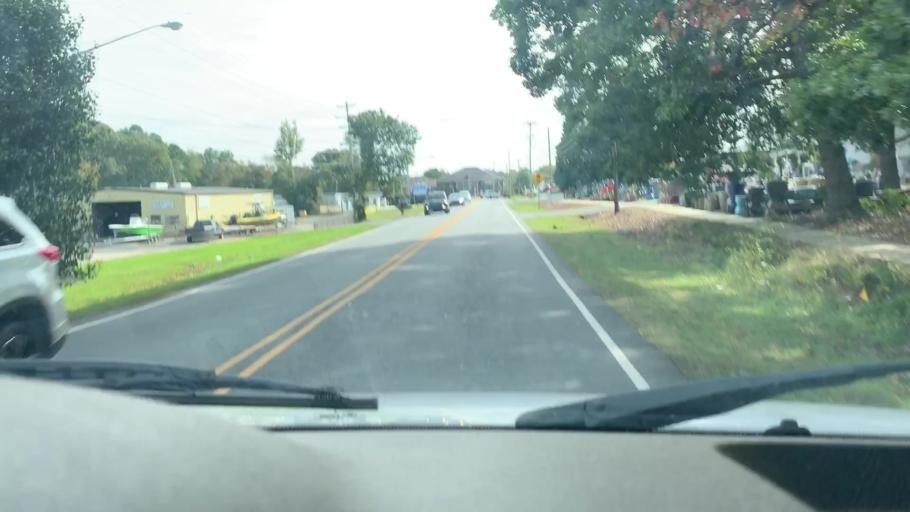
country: US
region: North Carolina
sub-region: Mecklenburg County
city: Cornelius
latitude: 35.4729
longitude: -80.8916
